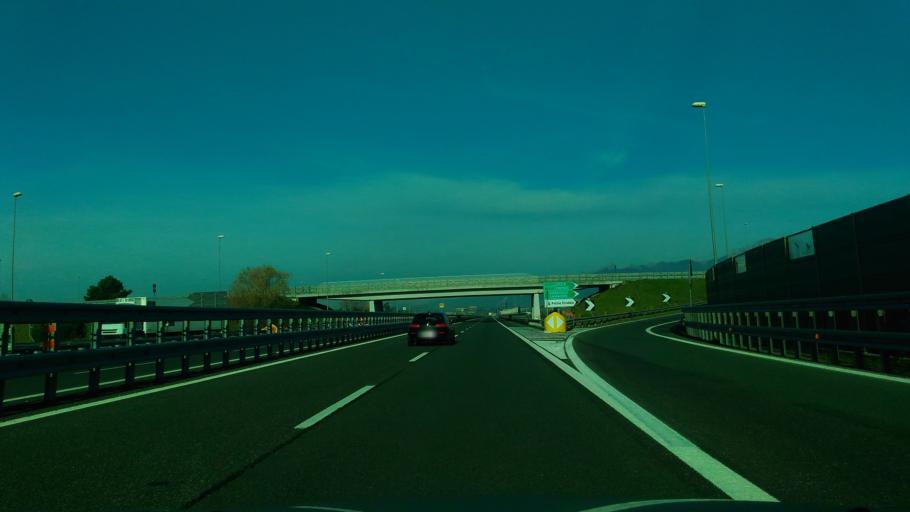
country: IT
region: Tuscany
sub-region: Provincia di Lucca
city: Viareggio
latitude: 43.8868
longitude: 10.2636
